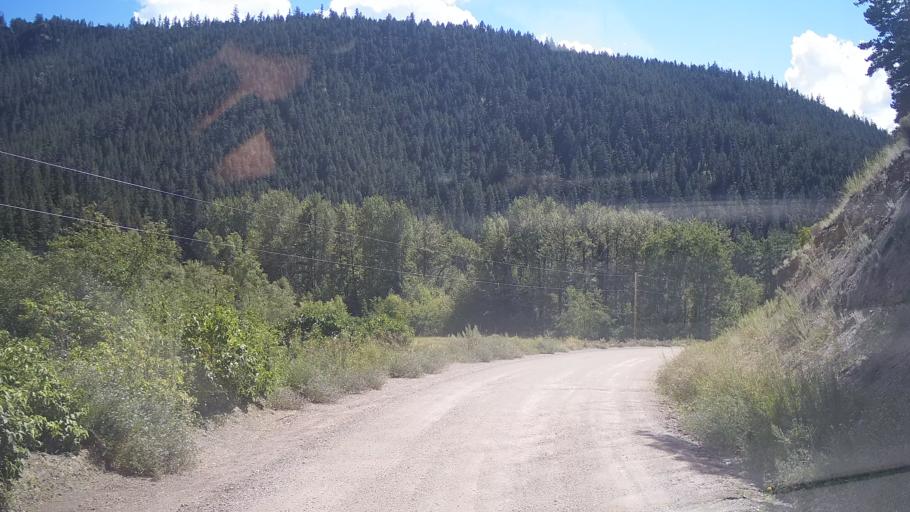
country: CA
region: British Columbia
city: Lillooet
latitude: 51.2480
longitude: -122.0278
